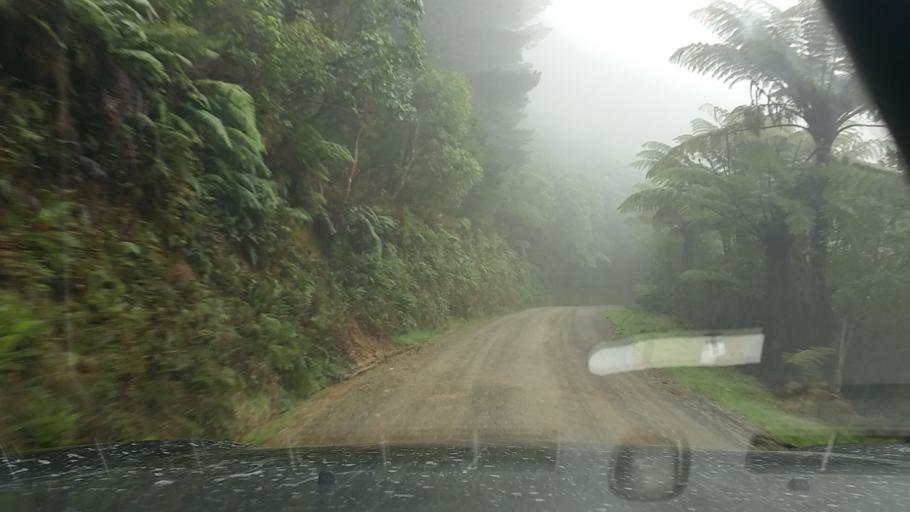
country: NZ
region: Marlborough
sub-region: Marlborough District
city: Picton
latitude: -41.1627
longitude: 173.9677
